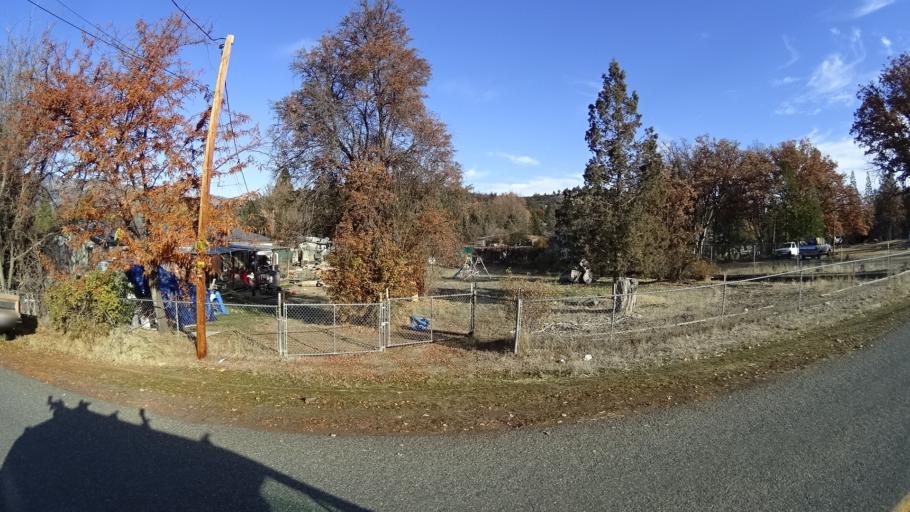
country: US
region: California
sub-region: Siskiyou County
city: Yreka
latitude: 41.6975
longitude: -122.6344
